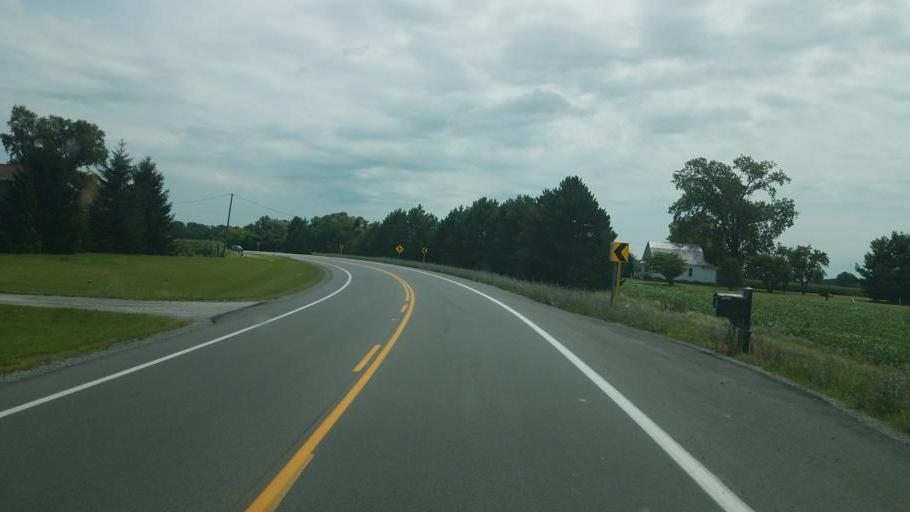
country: US
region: Ohio
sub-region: Wyandot County
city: Upper Sandusky
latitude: 40.8616
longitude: -83.2695
